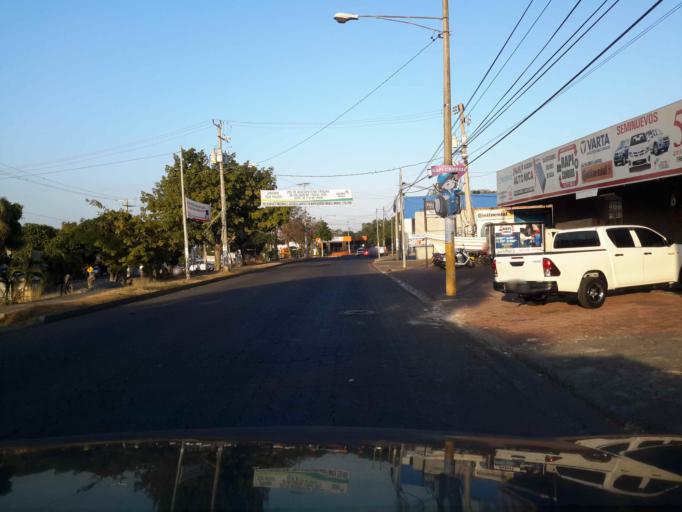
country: NI
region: Managua
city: Managua
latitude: 12.1458
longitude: -86.2889
